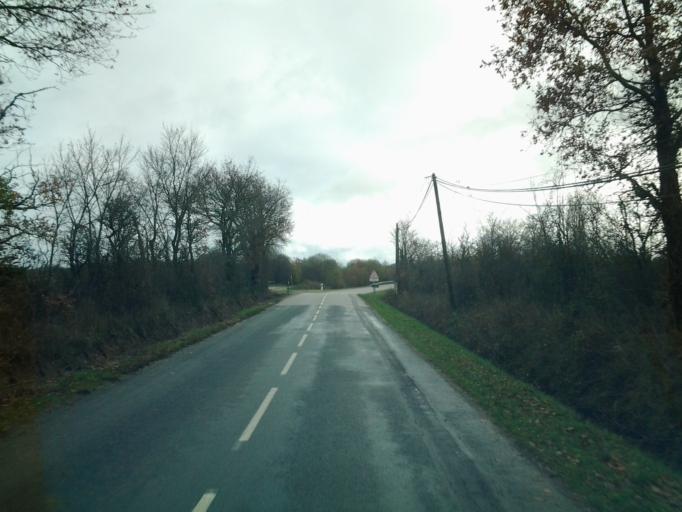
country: FR
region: Pays de la Loire
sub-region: Departement de la Vendee
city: La Roche-sur-Yon
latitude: 46.6544
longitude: -1.3891
